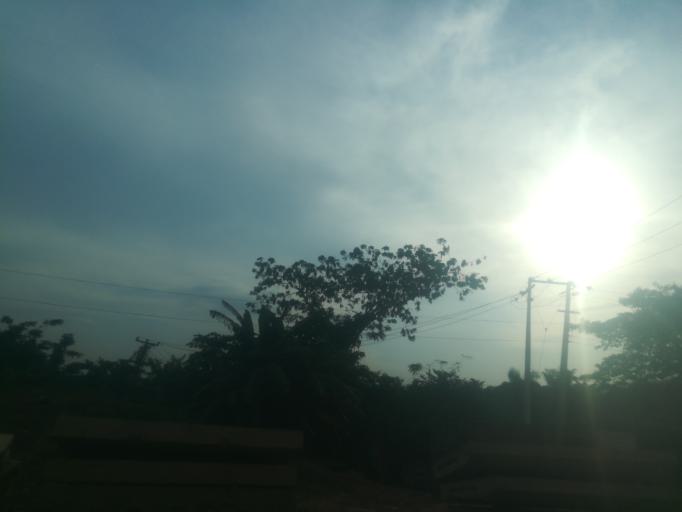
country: NG
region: Ogun
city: Abeokuta
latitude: 7.1584
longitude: 3.3235
